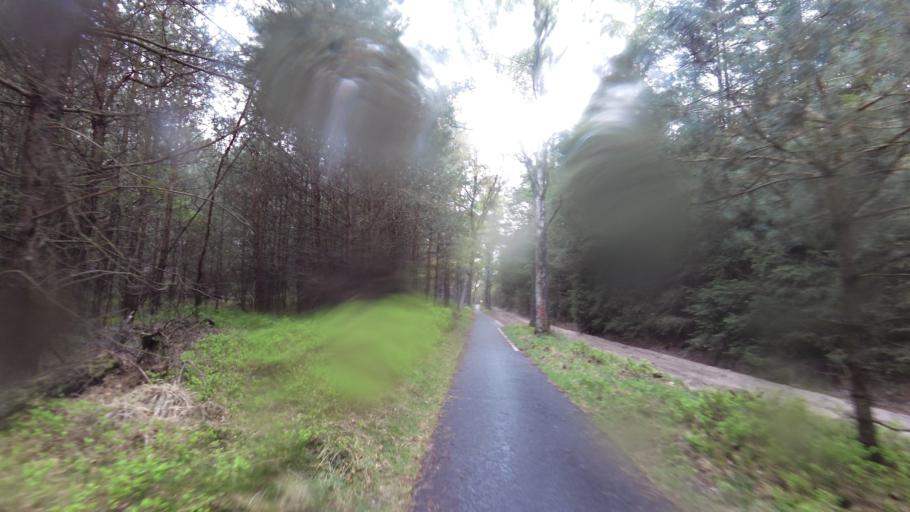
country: NL
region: Gelderland
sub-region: Gemeente Apeldoorn
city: Loenen
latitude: 52.0722
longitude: 6.0112
